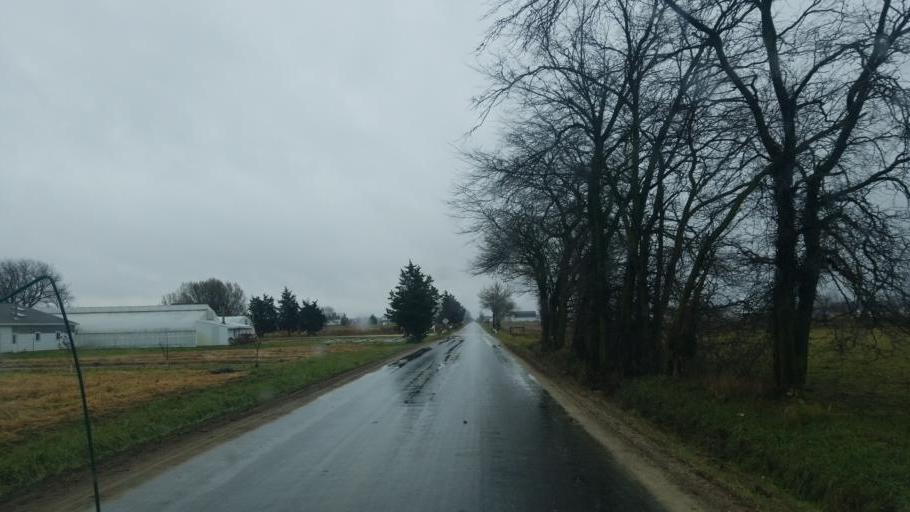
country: US
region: Indiana
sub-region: Adams County
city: Berne
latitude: 40.7165
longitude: -84.9174
